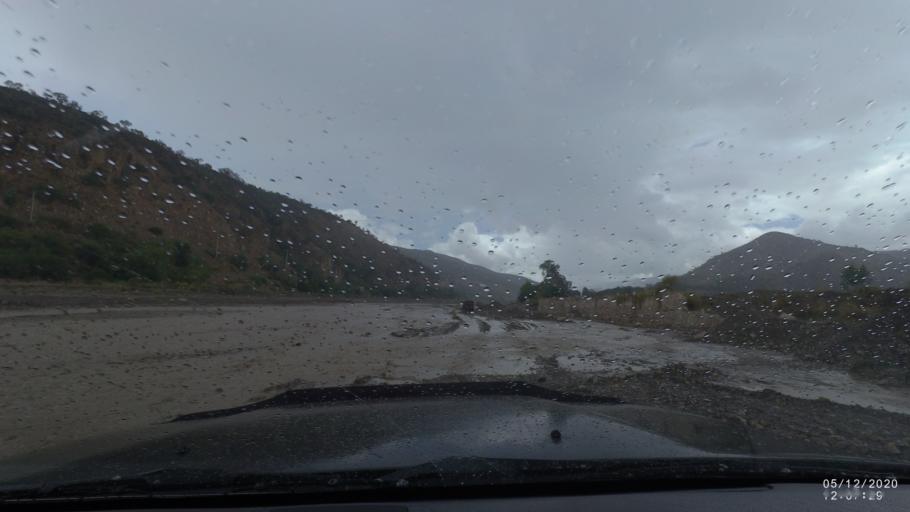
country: BO
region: Cochabamba
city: Sipe Sipe
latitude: -17.5722
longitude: -66.3646
